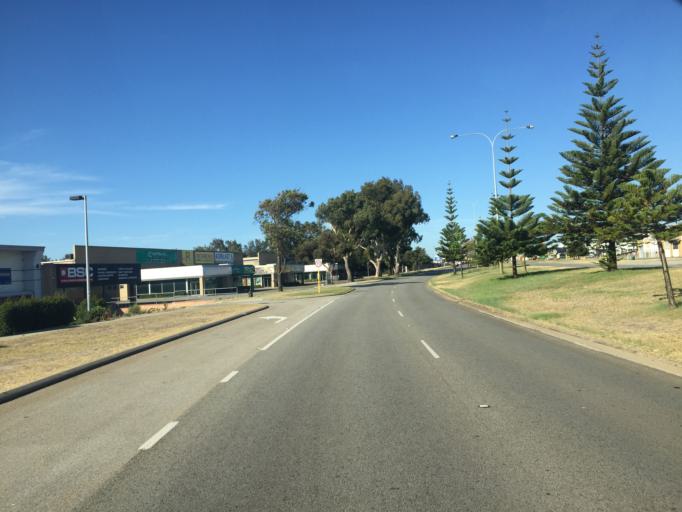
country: AU
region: Western Australia
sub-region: Canning
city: Queens Park
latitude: -31.9925
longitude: 115.9446
